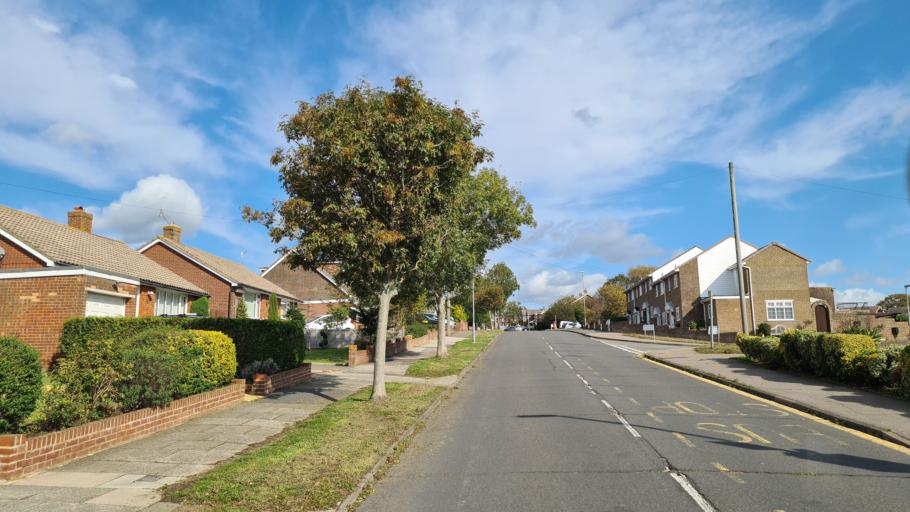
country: GB
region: England
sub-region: East Sussex
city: Hastings
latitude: 50.8781
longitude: 0.5684
